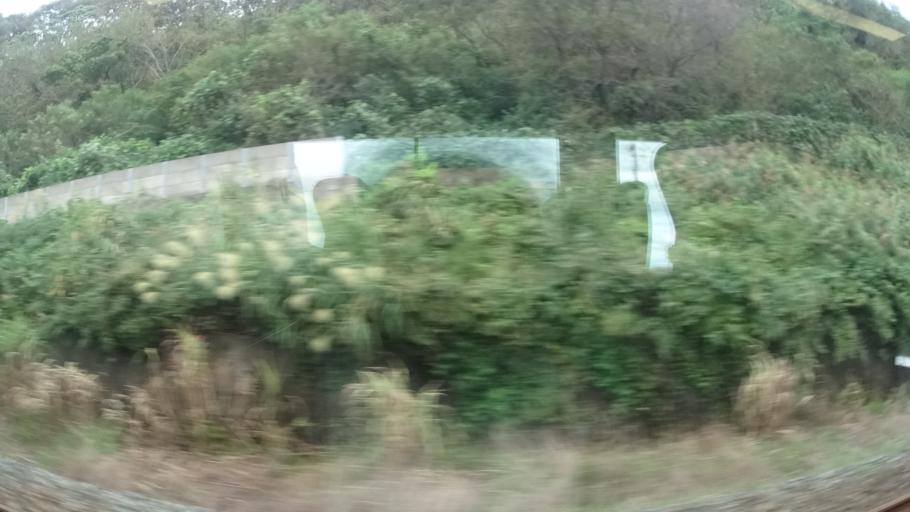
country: JP
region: Niigata
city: Murakami
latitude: 38.2650
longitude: 139.4472
